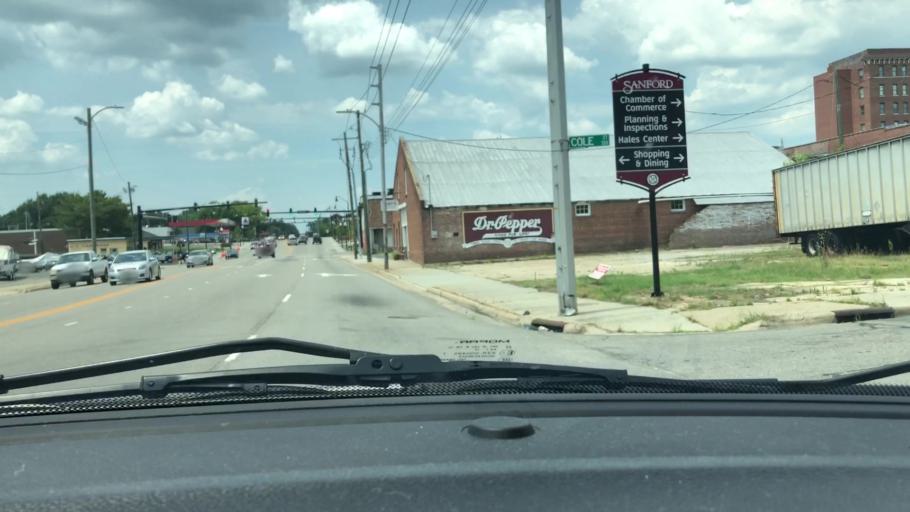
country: US
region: North Carolina
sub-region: Lee County
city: Sanford
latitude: 35.4779
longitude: -79.1786
